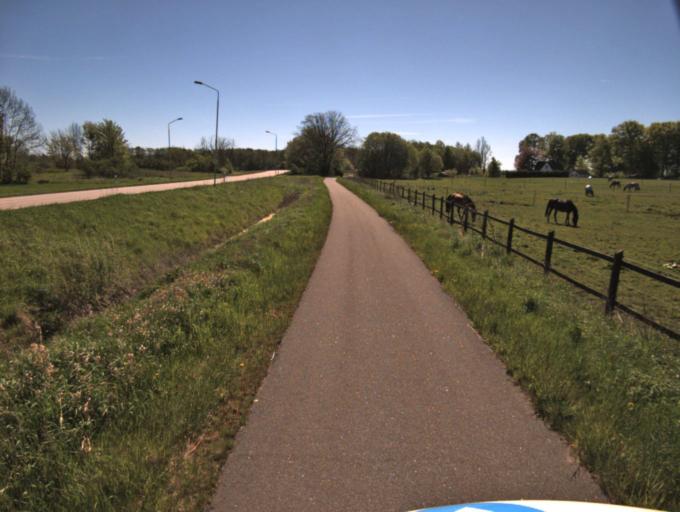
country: SE
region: Skane
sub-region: Kristianstads Kommun
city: Norra Asum
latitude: 55.9908
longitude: 14.1555
